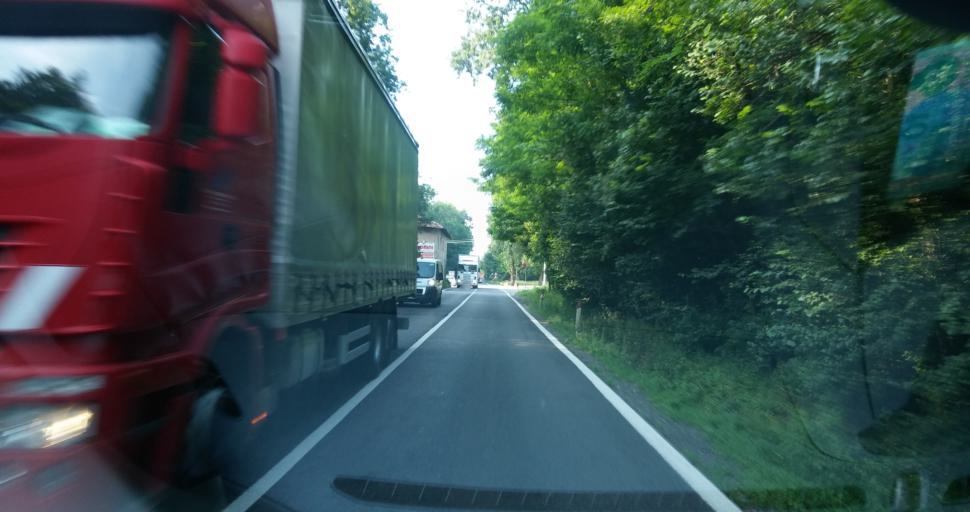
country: IT
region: Lombardy
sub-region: Provincia di Varese
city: Somma Lombardo
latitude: 45.6624
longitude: 8.7047
